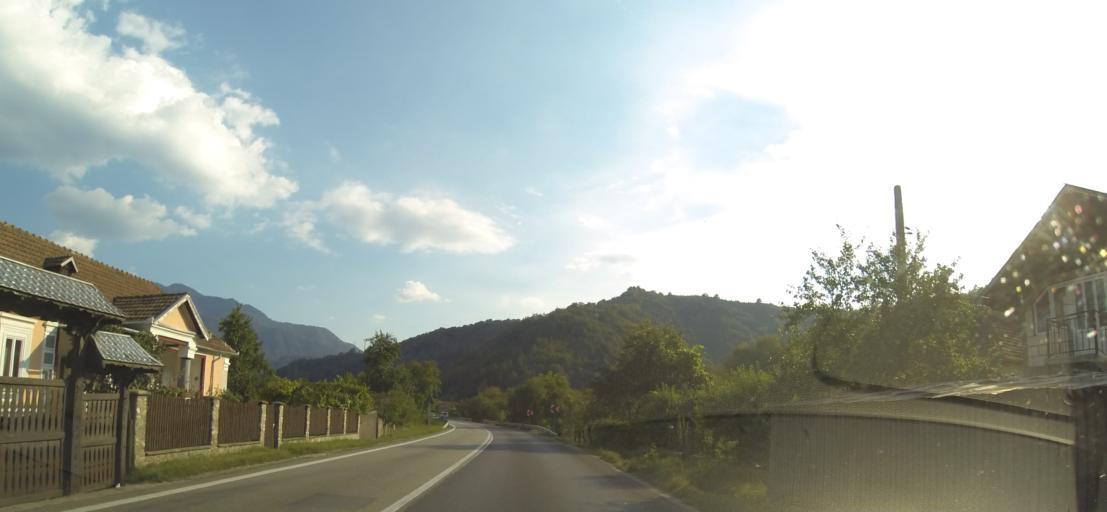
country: RO
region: Valcea
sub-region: Comuna Brezoi
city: Brezoi
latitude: 45.3690
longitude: 24.2913
